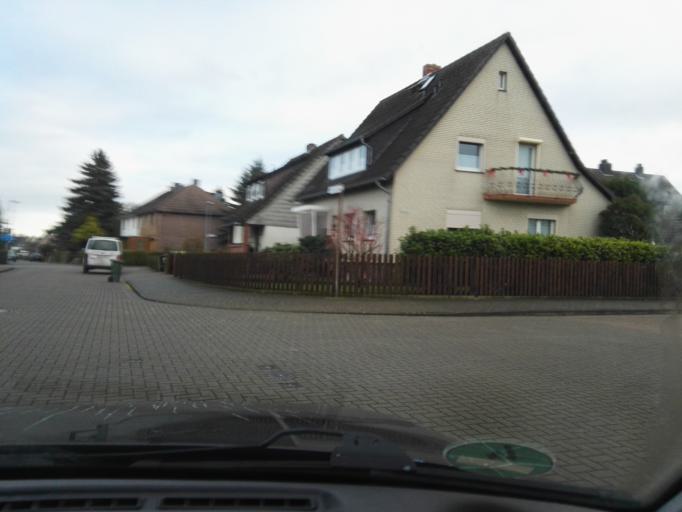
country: DE
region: Lower Saxony
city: Leiferde
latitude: 52.2343
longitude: 10.5004
